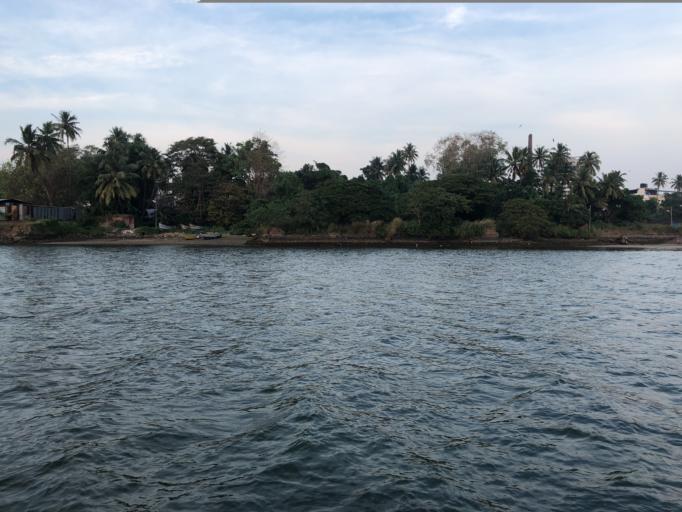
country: IN
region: Karnataka
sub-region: Dakshina Kannada
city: Ullal
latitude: 12.8430
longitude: 74.8408
